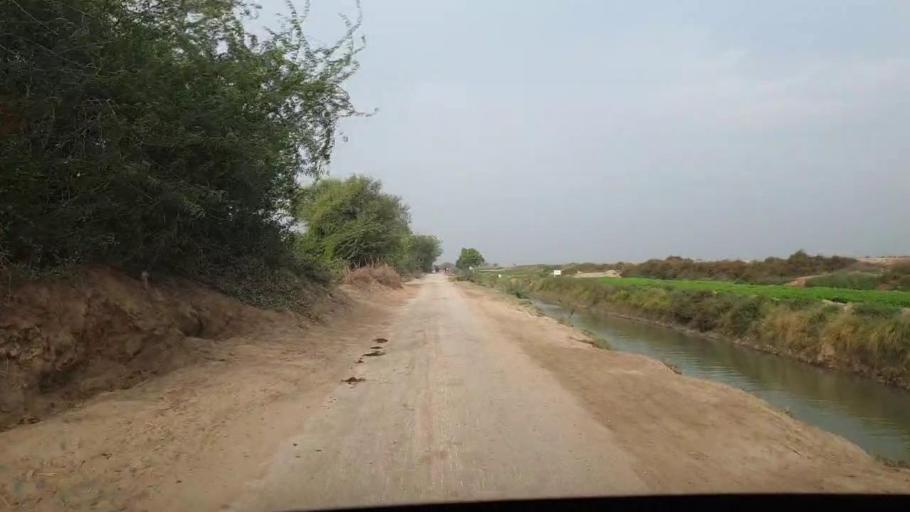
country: PK
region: Sindh
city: Chuhar Jamali
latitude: 24.3985
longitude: 67.9693
